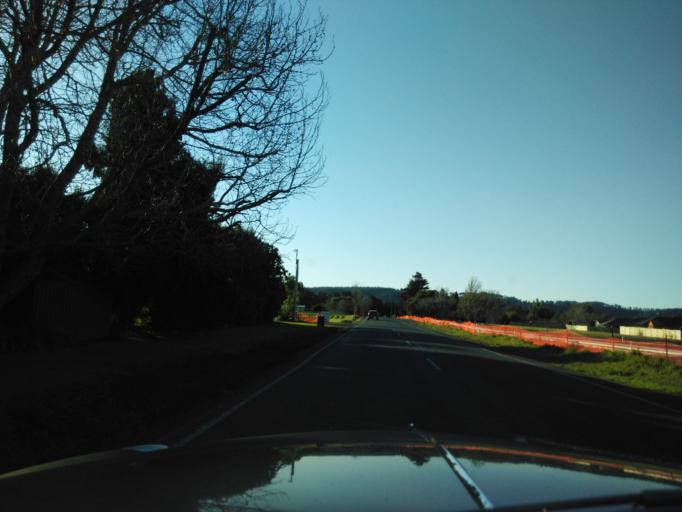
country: NZ
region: Auckland
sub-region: Auckland
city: Rosebank
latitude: -36.7656
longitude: 174.5874
